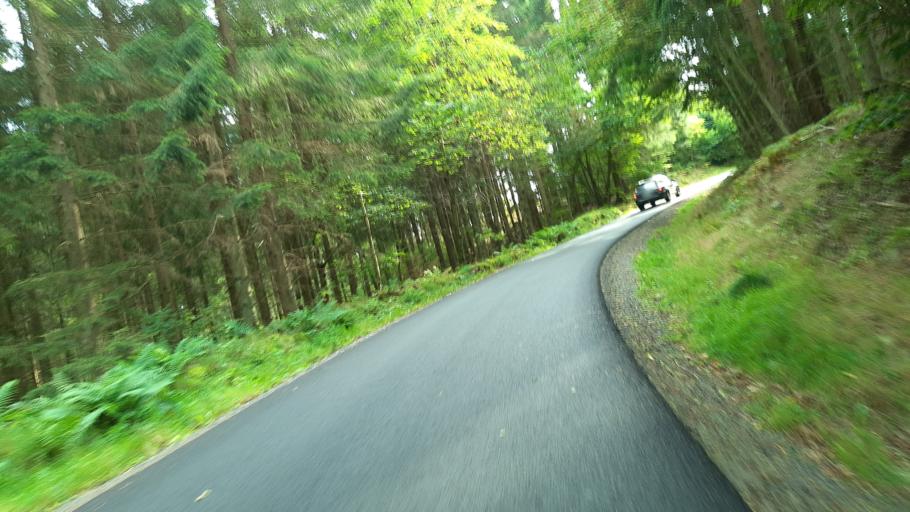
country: SE
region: Blekinge
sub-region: Karlskrona Kommun
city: Nattraby
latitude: 56.2541
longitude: 15.5103
